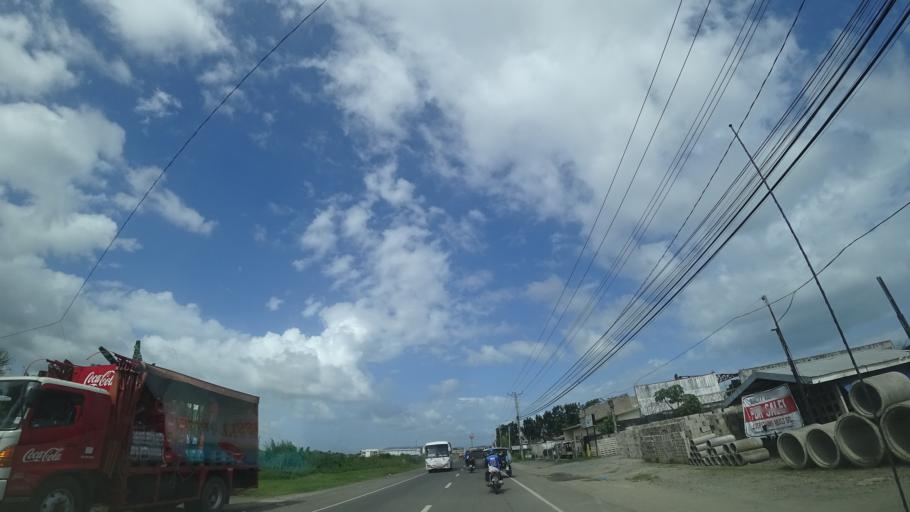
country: PH
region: Eastern Visayas
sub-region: Province of Leyte
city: Pawing
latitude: 11.1739
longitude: 125.0000
